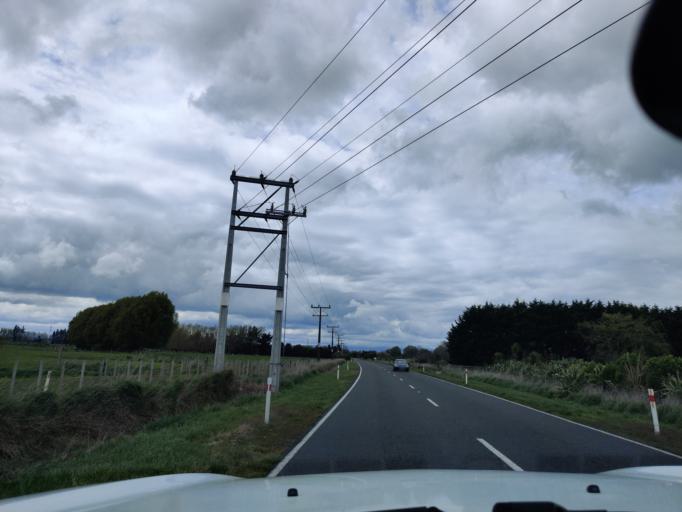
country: NZ
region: Manawatu-Wanganui
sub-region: Palmerston North City
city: Palmerston North
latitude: -40.2462
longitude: 175.5444
